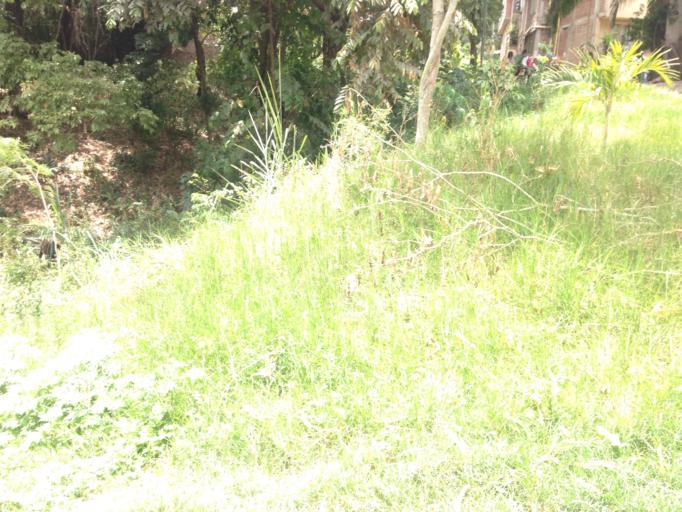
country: CO
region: Valle del Cauca
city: Cali
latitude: 3.4884
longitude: -76.5321
